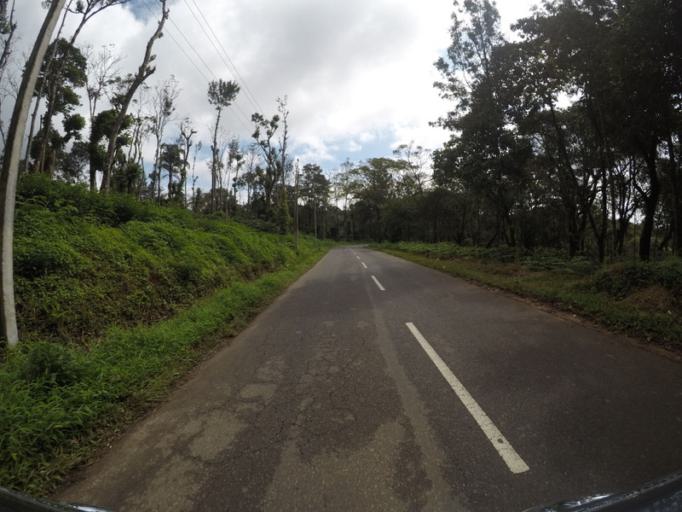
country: IN
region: Karnataka
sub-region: Kodagu
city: Madikeri
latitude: 12.4556
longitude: 75.7635
